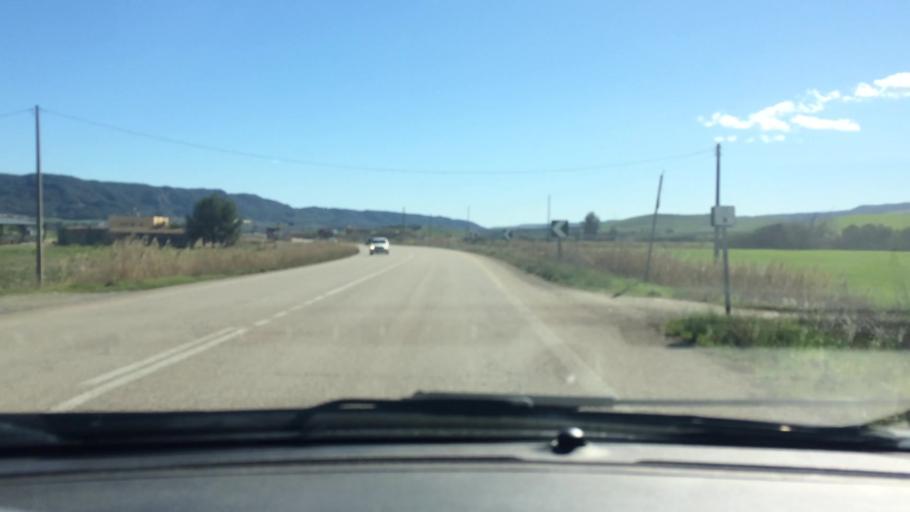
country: IT
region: Basilicate
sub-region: Provincia di Matera
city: Montescaglioso
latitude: 40.5332
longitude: 16.6076
